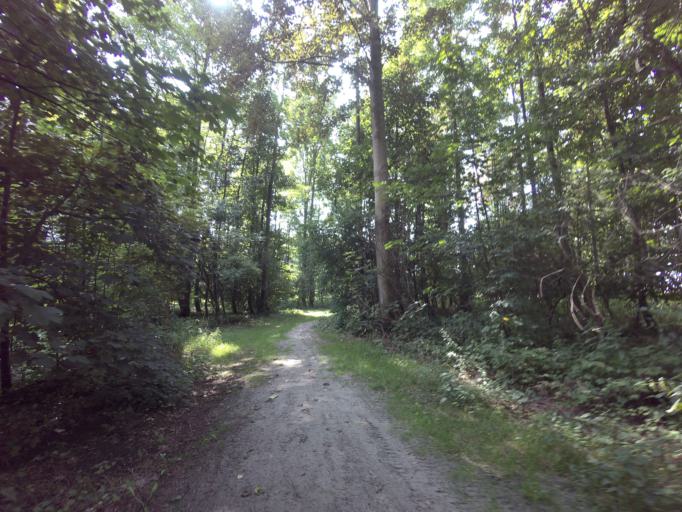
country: NL
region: North Holland
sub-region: Gemeente Huizen
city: Huizen
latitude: 52.3232
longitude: 5.2886
